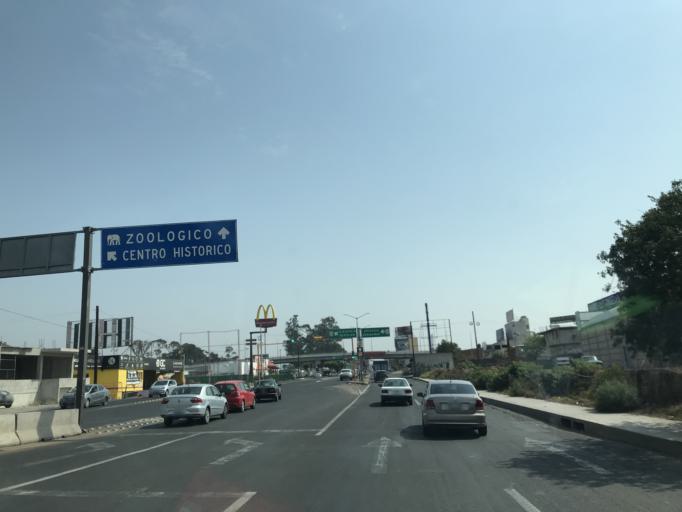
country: MX
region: Tlaxcala
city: Tlaxcala de Xicohtencatl
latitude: 19.3156
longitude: -98.2043
